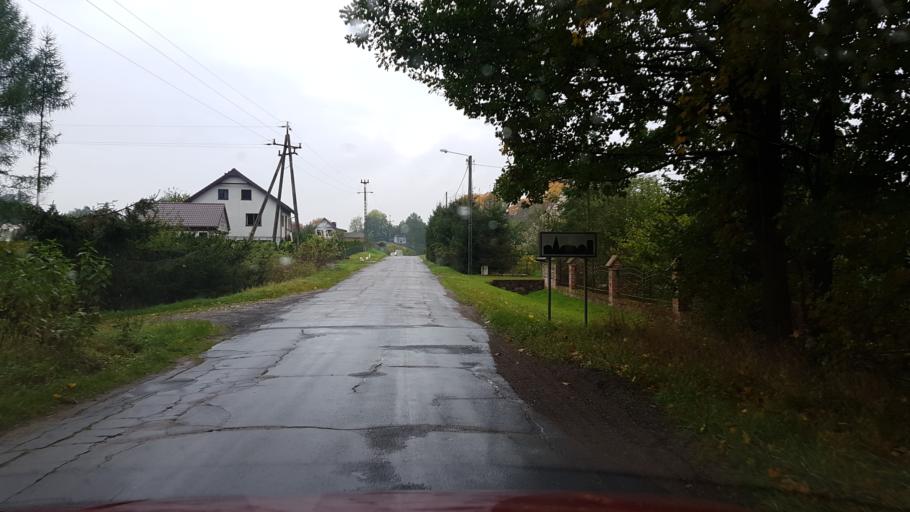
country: PL
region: West Pomeranian Voivodeship
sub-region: Powiat walecki
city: Walcz
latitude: 53.3705
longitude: 16.4335
